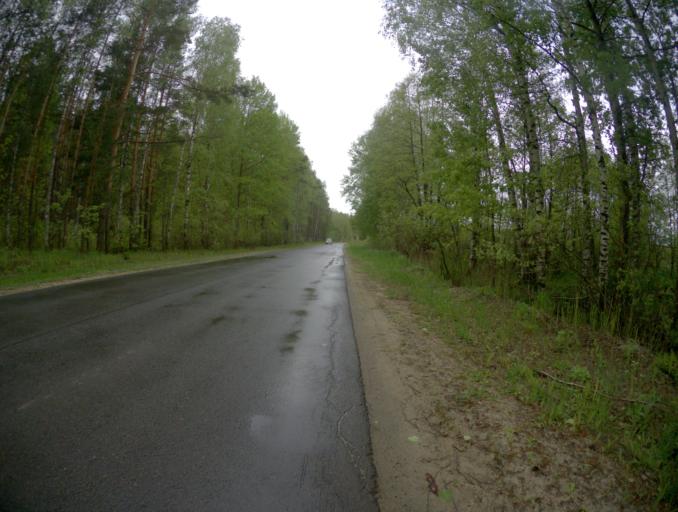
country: RU
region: Vladimir
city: Zolotkovo
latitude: 55.3388
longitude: 41.0073
